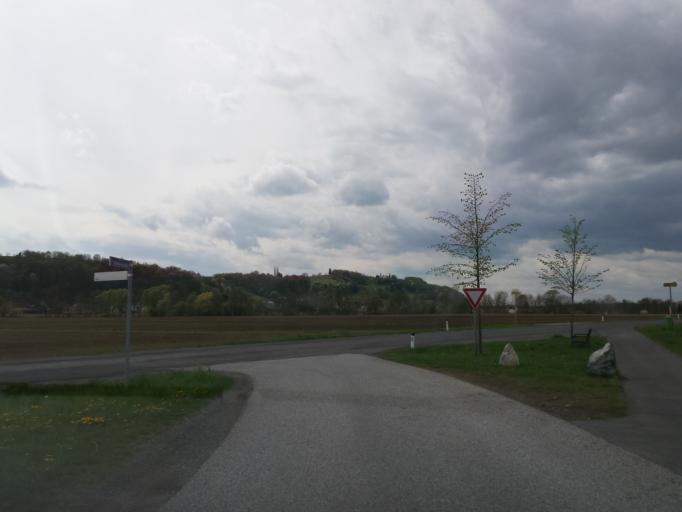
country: AT
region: Styria
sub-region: Politischer Bezirk Hartberg-Fuerstenfeld
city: Loipersdorf bei Fuerstenfeld
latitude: 47.0126
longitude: 16.1151
